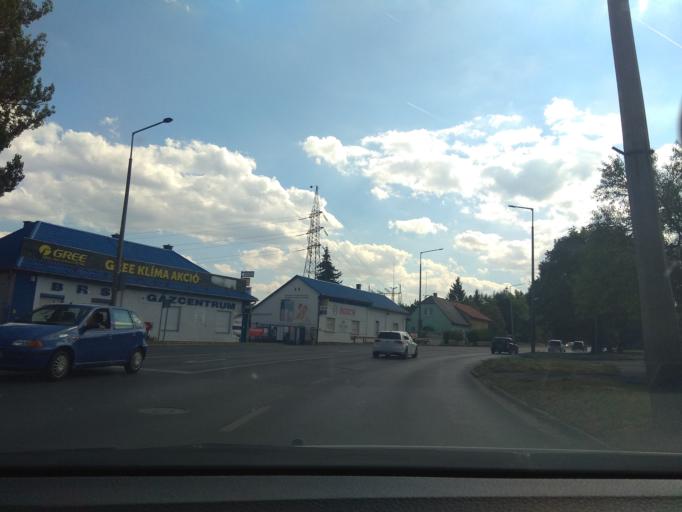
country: HU
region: Borsod-Abauj-Zemplen
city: Miskolc
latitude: 48.0875
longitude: 20.7917
